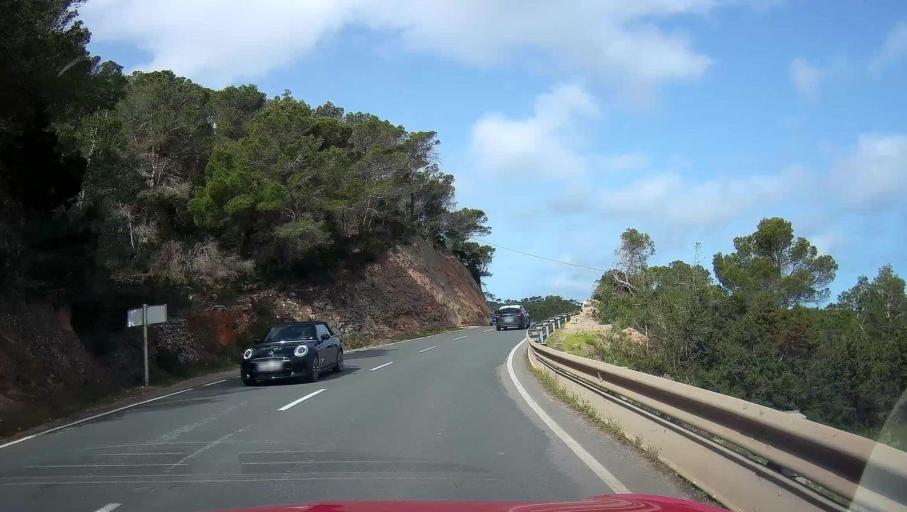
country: ES
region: Balearic Islands
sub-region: Illes Balears
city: Sant Joan de Labritja
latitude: 39.0995
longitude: 1.5030
